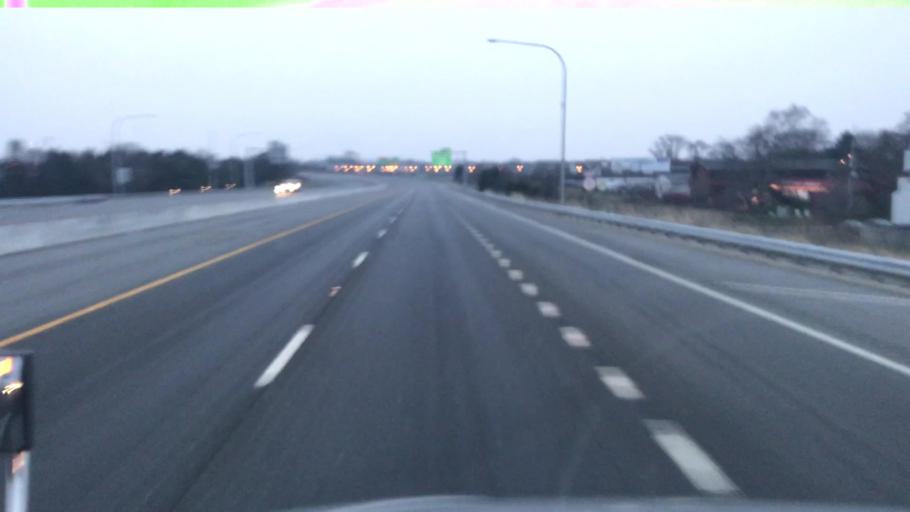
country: US
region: Delaware
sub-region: Kent County
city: Dover Base Housing
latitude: 39.1292
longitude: -75.4912
